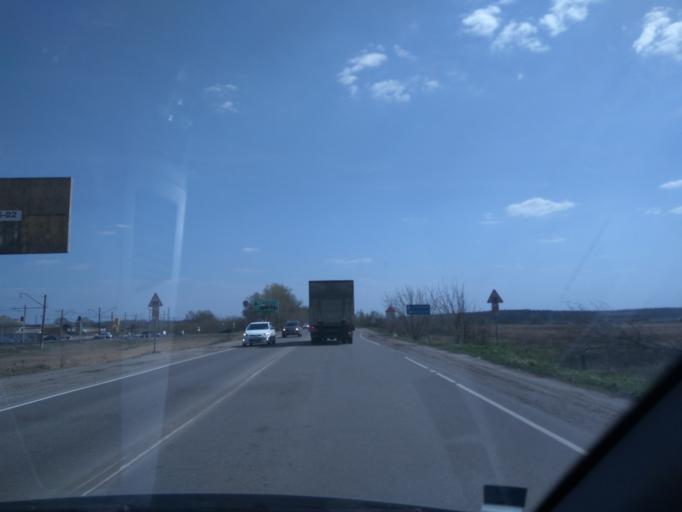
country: RU
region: Moskovskaya
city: Ramenskoye
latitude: 55.5458
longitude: 38.2782
